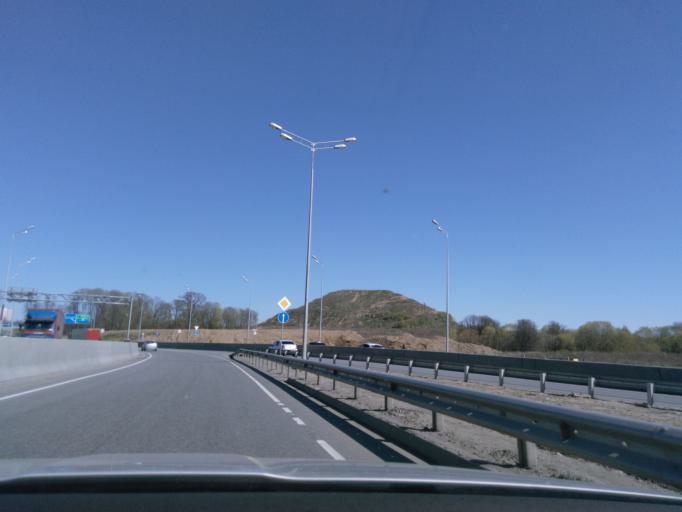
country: RU
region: Moscow
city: Businovo
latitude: 55.8945
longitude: 37.4945
